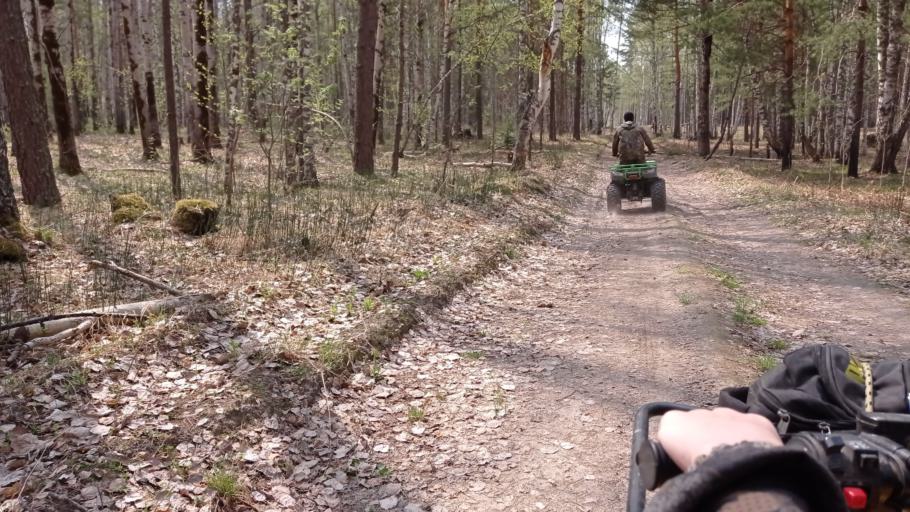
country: RU
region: Tomsk
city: Timiryazevskoye
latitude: 56.4352
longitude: 84.6481
